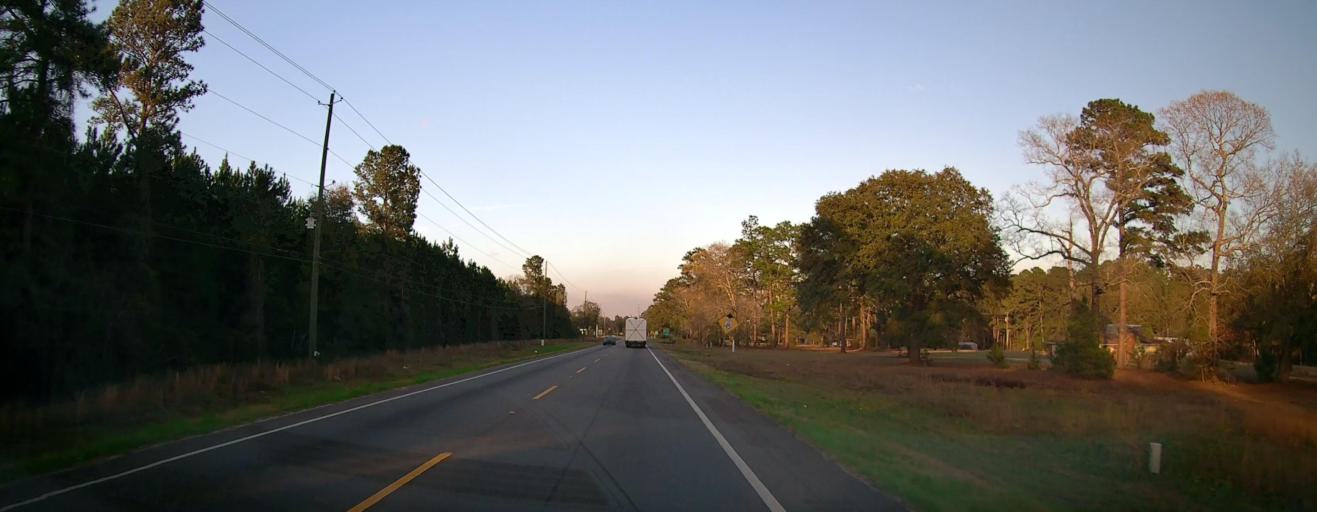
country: US
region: Georgia
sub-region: Effingham County
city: Guyton
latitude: 32.1937
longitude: -81.4421
